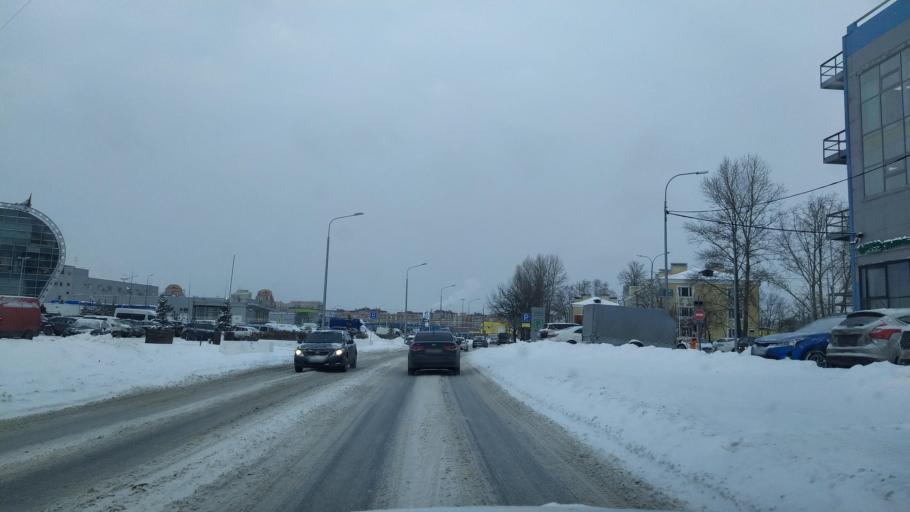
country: RU
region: St.-Petersburg
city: Komendantsky aerodrom
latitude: 59.9965
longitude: 30.2712
